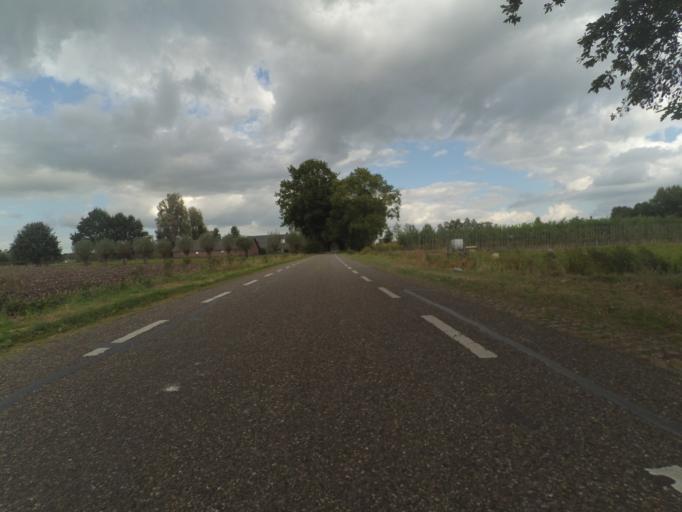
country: NL
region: Utrecht
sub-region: Gemeente Utrechtse Heuvelrug
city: Overberg
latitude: 52.0603
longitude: 5.5192
